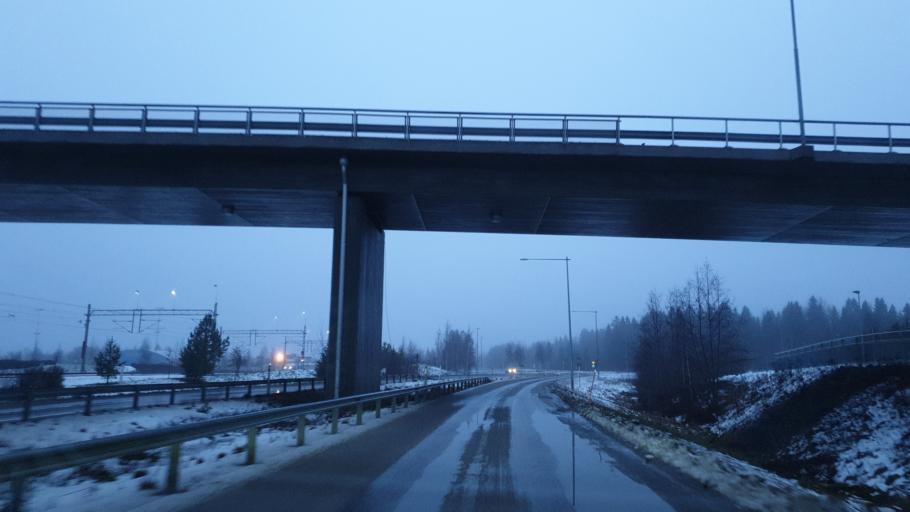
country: SE
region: Vaesterbotten
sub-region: Umea Kommun
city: Umea
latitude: 63.7903
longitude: 20.3140
